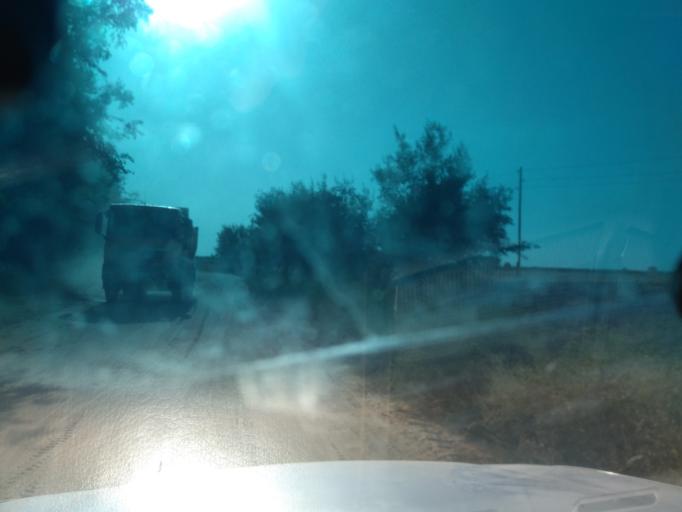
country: TJ
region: Viloyati Sughd
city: Buston
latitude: 40.5540
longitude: 69.0740
